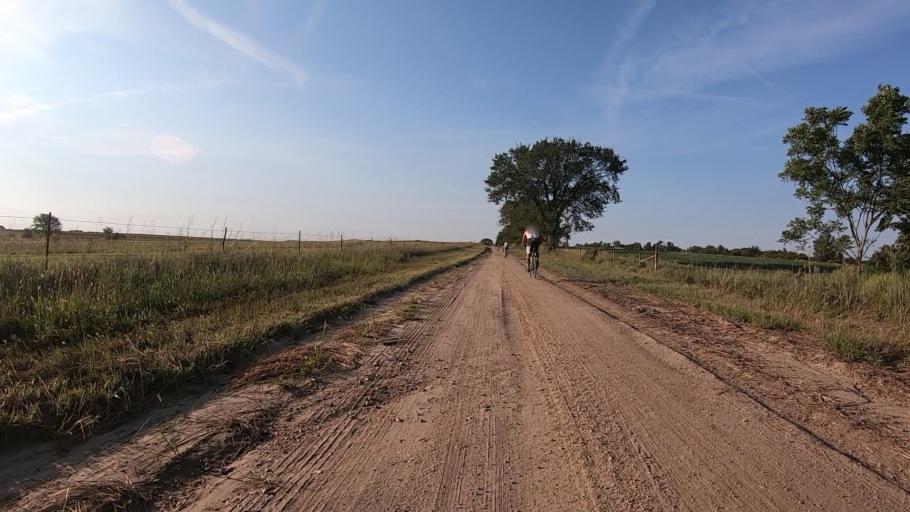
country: US
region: Kansas
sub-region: Marshall County
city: Blue Rapids
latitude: 39.7154
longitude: -96.8067
